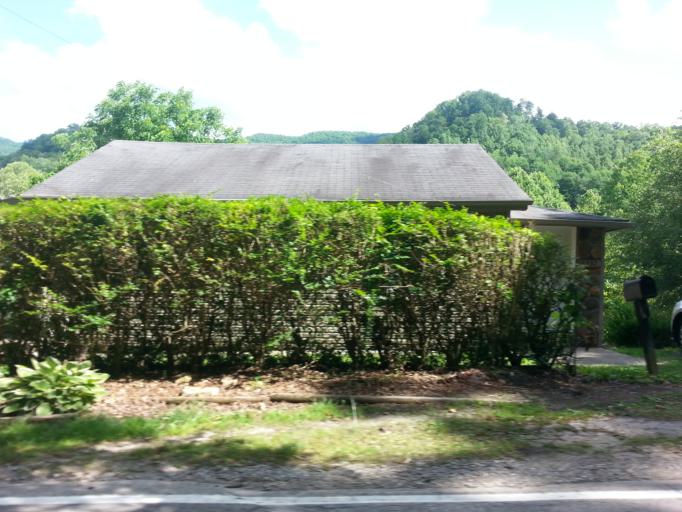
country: US
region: Kentucky
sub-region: Harlan County
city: Harlan
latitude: 36.9034
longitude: -83.2409
